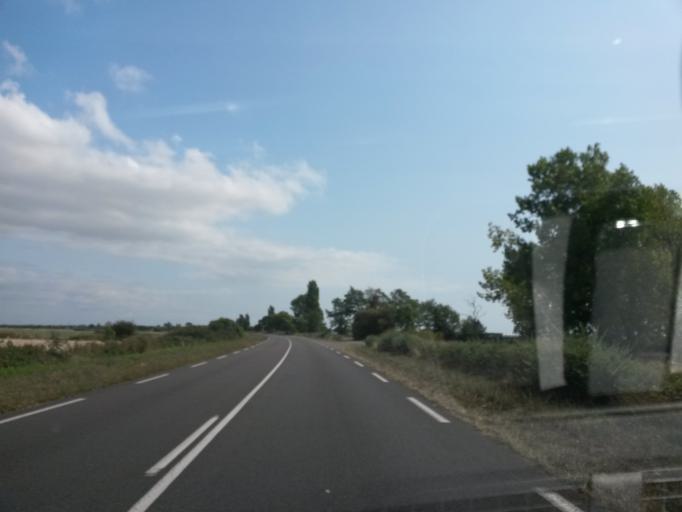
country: FR
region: Pays de la Loire
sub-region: Departement de la Vendee
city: La Tranche-sur-Mer
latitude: 46.3577
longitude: -1.4443
